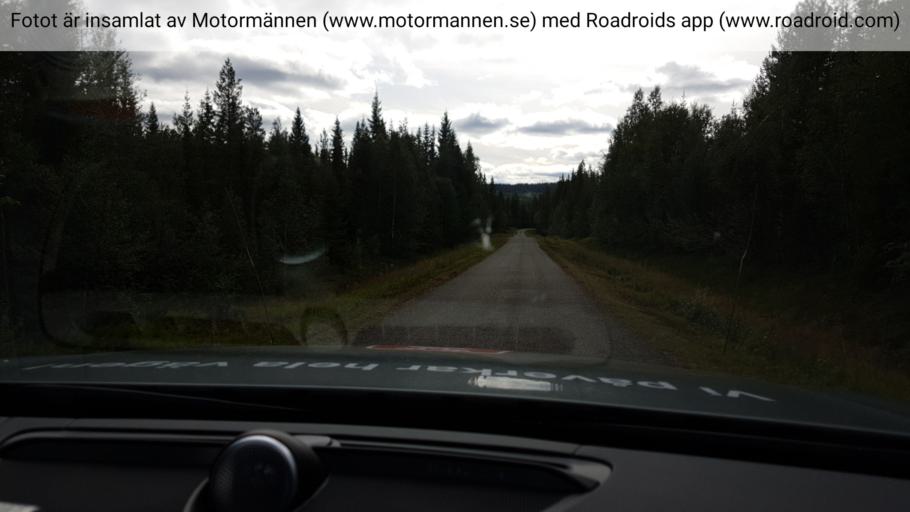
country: SE
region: Jaemtland
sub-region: Stroemsunds Kommun
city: Stroemsund
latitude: 64.5361
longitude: 15.2996
